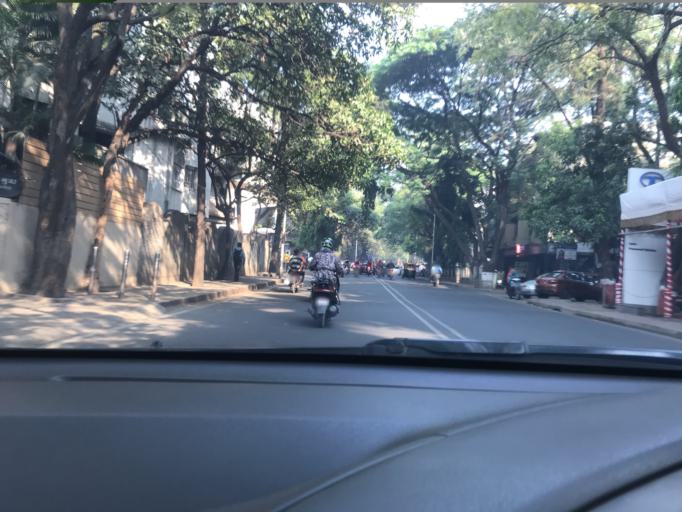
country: IN
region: Maharashtra
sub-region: Pune Division
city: Pune
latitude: 18.5111
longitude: 73.8294
